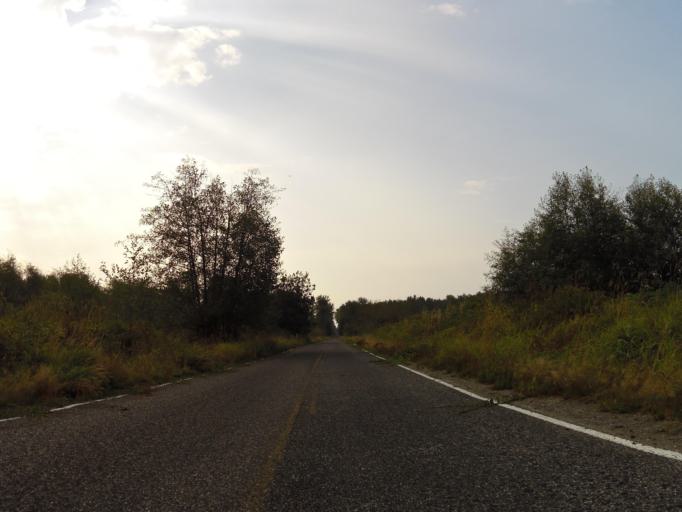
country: US
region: Washington
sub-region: Whatcom County
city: Birch Bay
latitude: 48.8775
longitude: -122.7320
